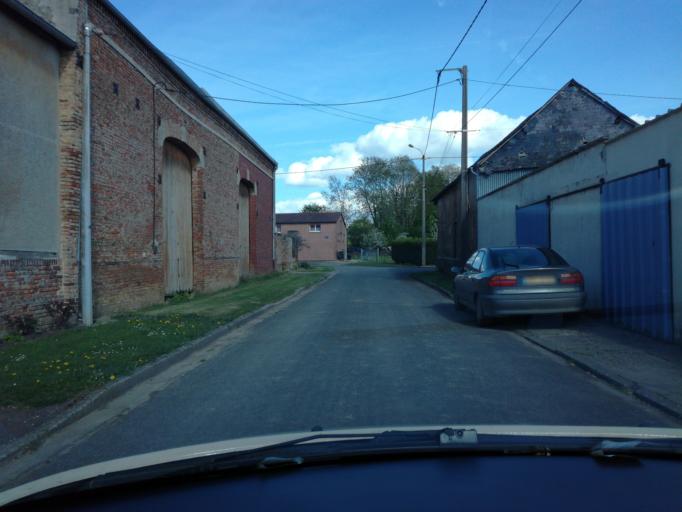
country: FR
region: Picardie
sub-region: Departement de la Somme
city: Hornoy-le-Bourg
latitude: 49.8291
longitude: 1.9357
